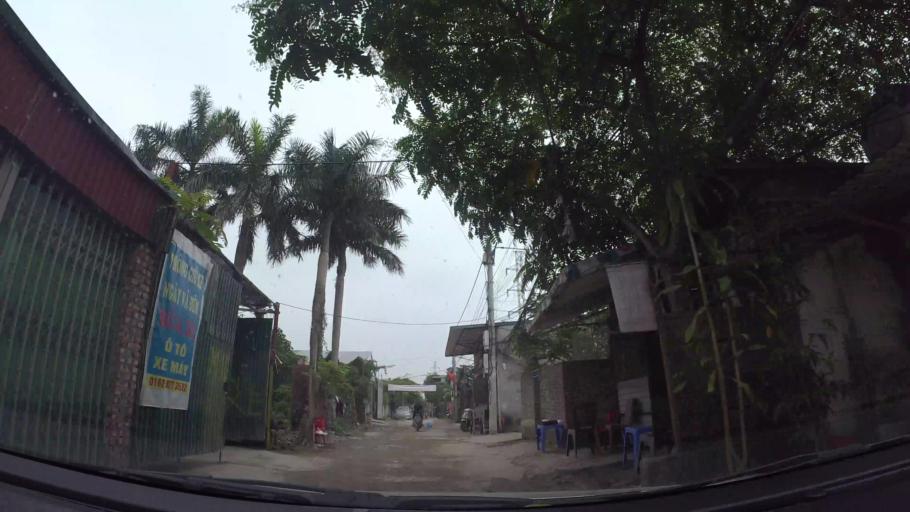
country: VN
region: Ha Noi
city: Tay Ho
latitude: 21.0702
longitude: 105.8313
